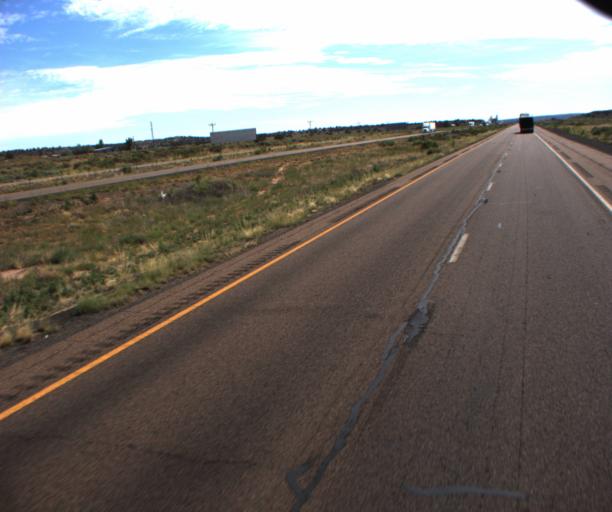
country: US
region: Arizona
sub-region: Apache County
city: Houck
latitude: 35.2044
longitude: -109.3691
